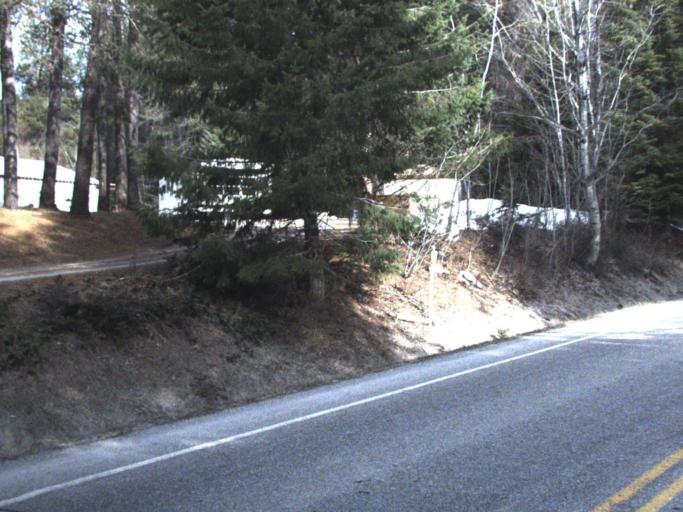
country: US
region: Washington
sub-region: Pend Oreille County
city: Newport
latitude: 48.4455
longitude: -117.3222
